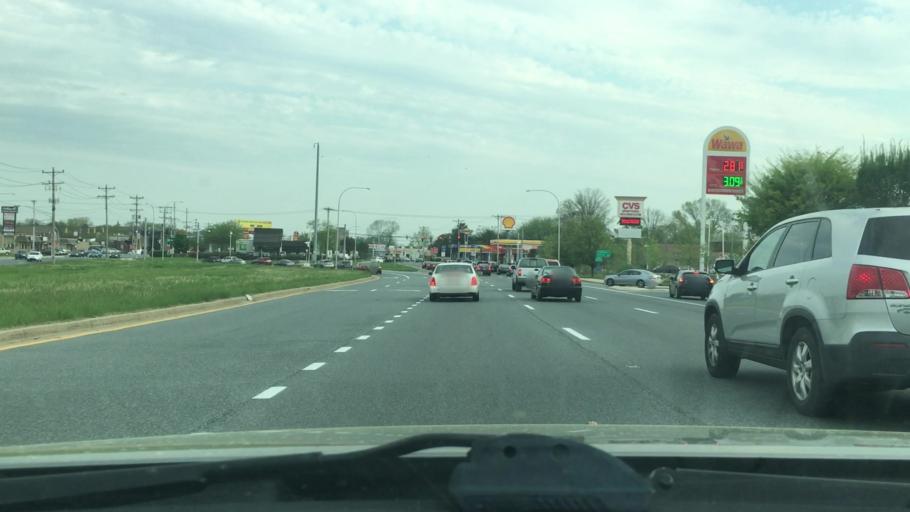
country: US
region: Delaware
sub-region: New Castle County
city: Greenville
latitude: 39.8109
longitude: -75.5501
